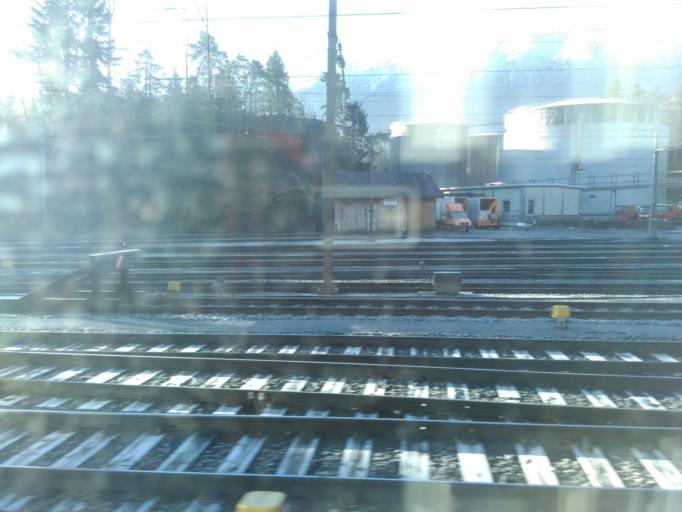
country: CH
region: Schwyz
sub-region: Bezirk Schwyz
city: Goldau
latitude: 47.0487
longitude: 8.5572
